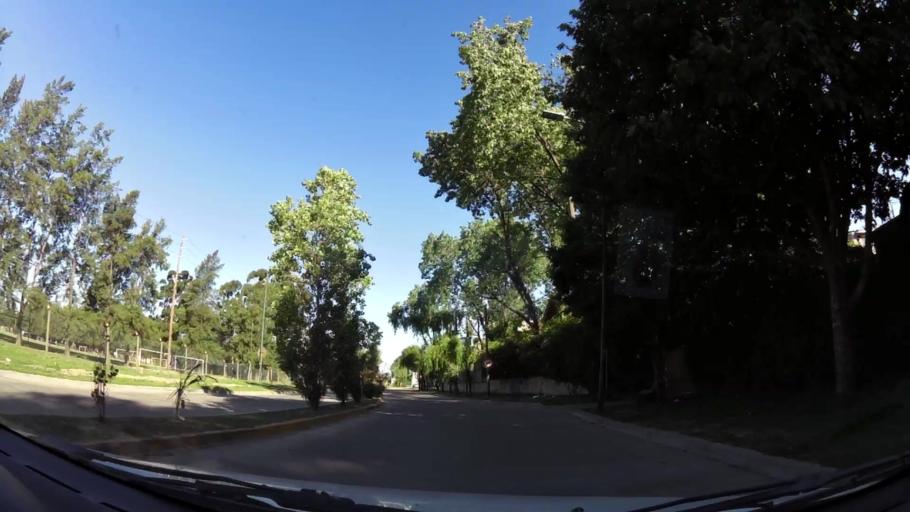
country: AR
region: Buenos Aires
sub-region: Partido de San Isidro
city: San Isidro
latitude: -34.4646
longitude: -58.5036
